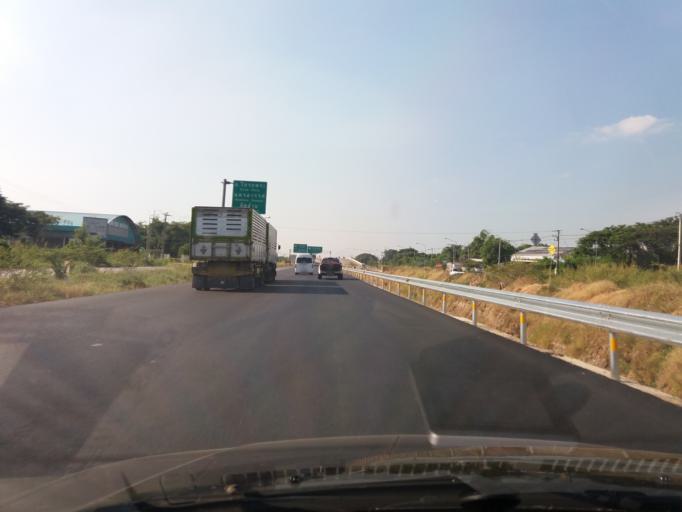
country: TH
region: Nakhon Sawan
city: Krok Phra
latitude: 15.6296
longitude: 100.1054
